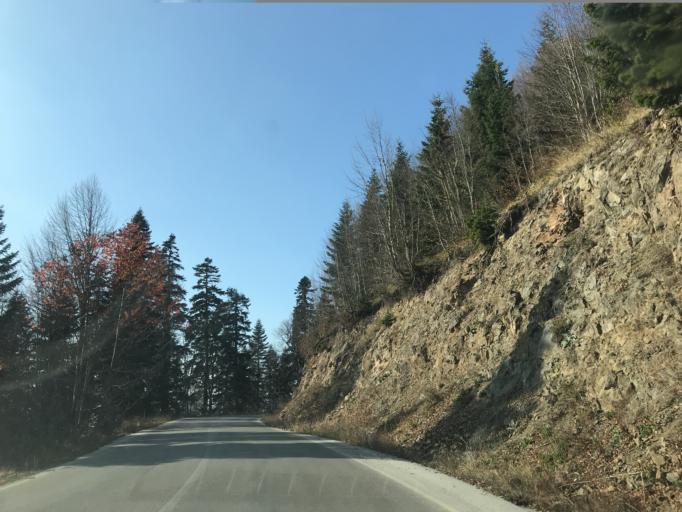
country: TR
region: Bolu
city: Bolu
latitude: 40.8867
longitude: 31.6816
